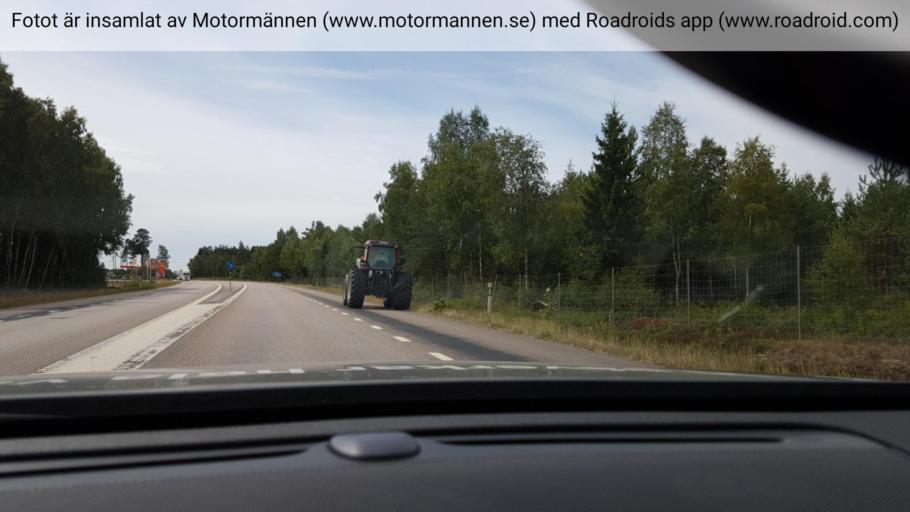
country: SE
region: Vaestra Goetaland
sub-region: Vara Kommun
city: Vara
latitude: 58.2192
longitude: 12.9146
